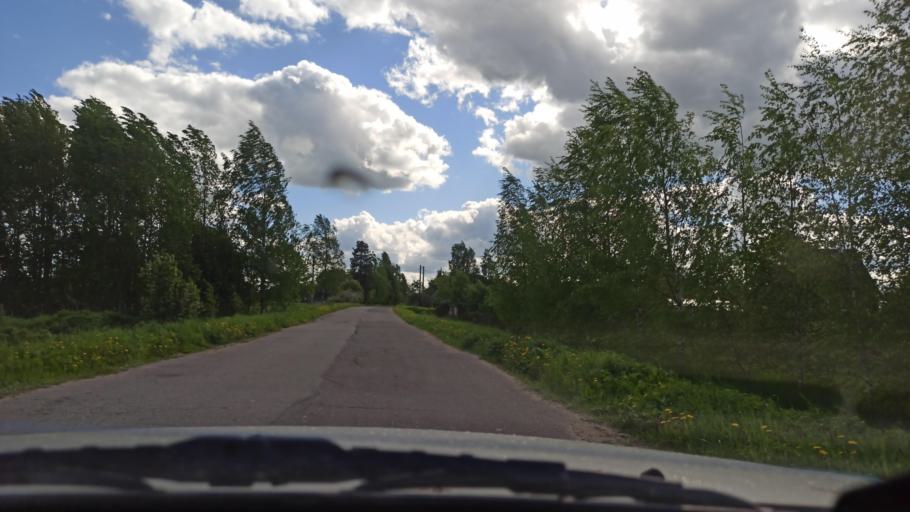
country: RU
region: Vologda
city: Molochnoye
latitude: 59.3799
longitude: 39.7190
